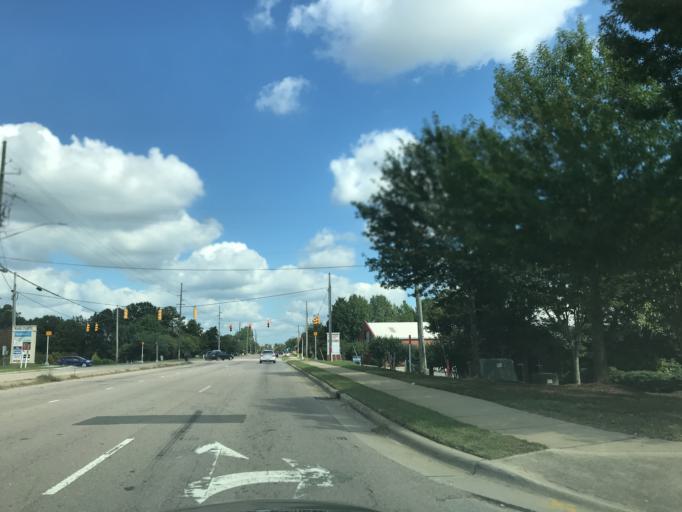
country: US
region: North Carolina
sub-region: Wake County
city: Wake Forest
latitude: 35.9477
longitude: -78.5351
